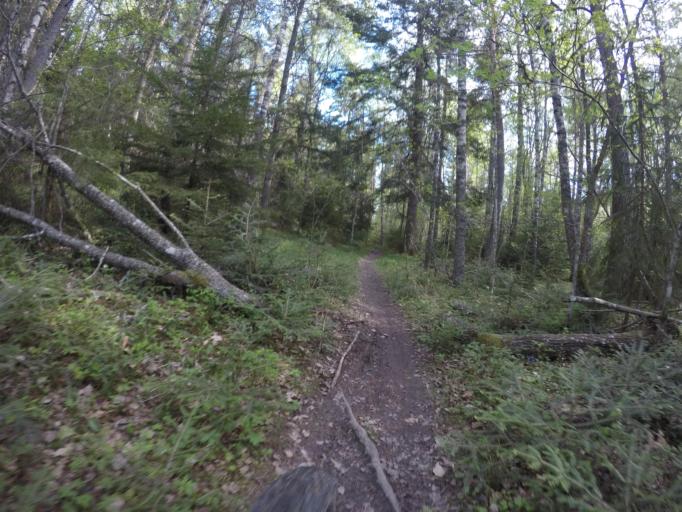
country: SE
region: Vaestmanland
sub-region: Vasteras
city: Vasteras
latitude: 59.6577
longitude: 16.5066
